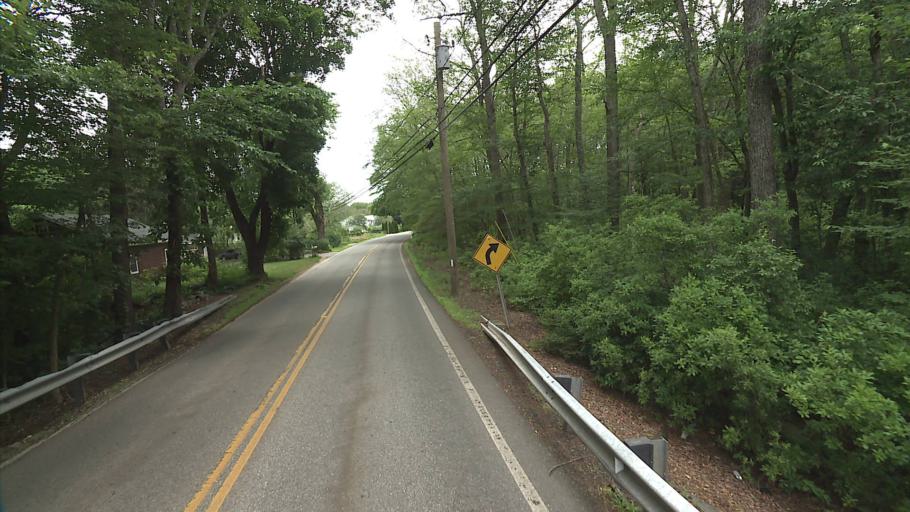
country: US
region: Connecticut
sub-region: New London County
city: Ledyard Center
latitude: 41.4468
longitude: -72.0092
